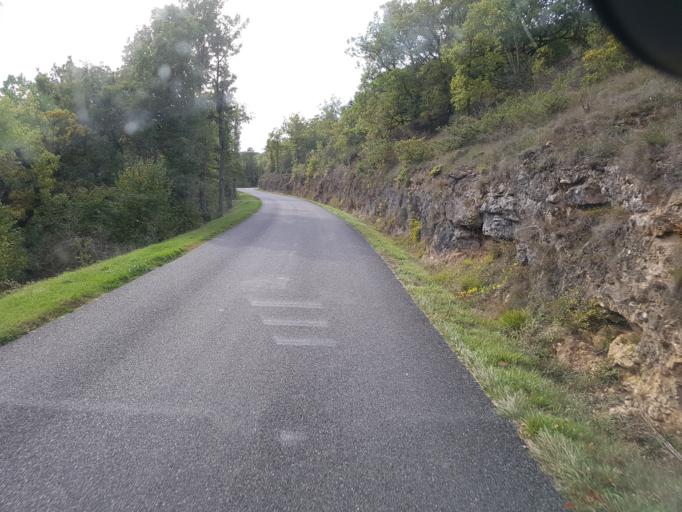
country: FR
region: Midi-Pyrenees
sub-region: Departement de l'Aveyron
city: Saint-Georges-de-Luzencon
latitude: 44.0024
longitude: 2.9550
